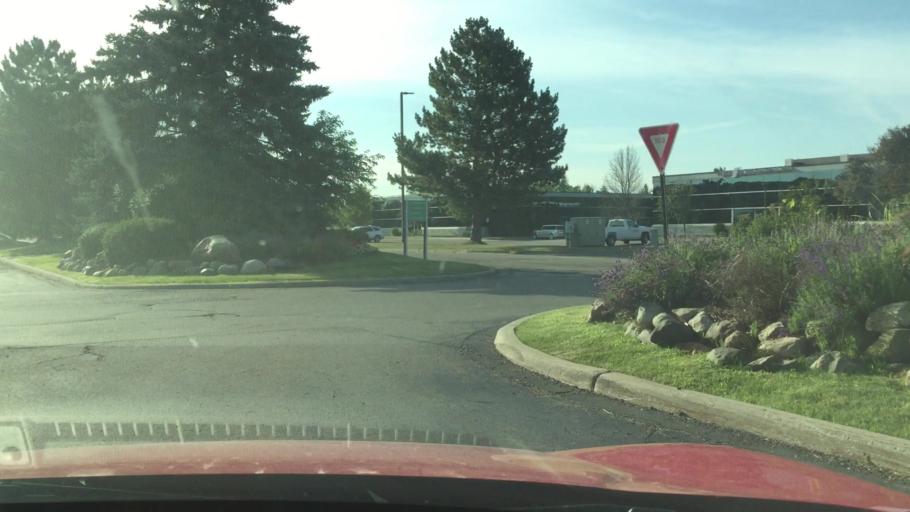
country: US
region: Michigan
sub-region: Genesee County
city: Flint
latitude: 42.9464
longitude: -83.7206
